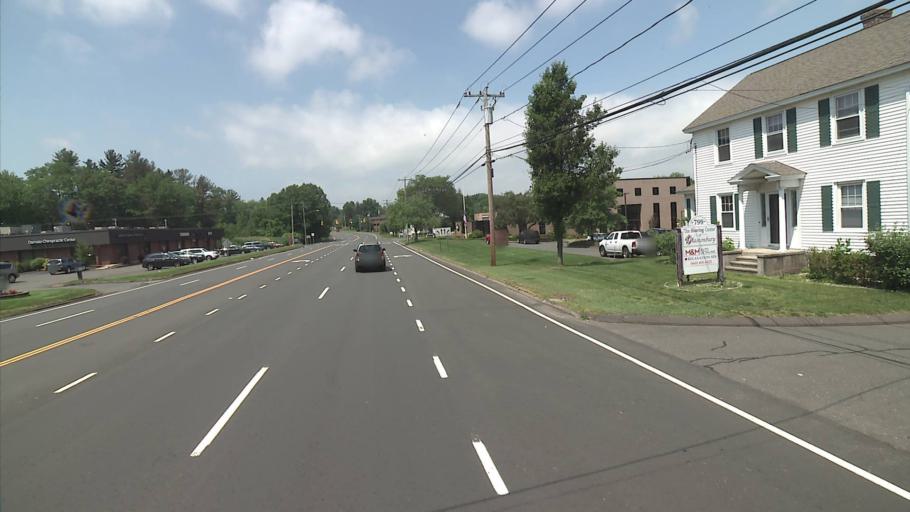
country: US
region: Connecticut
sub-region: Hartford County
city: Glastonbury Center
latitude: 41.7159
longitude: -72.5834
